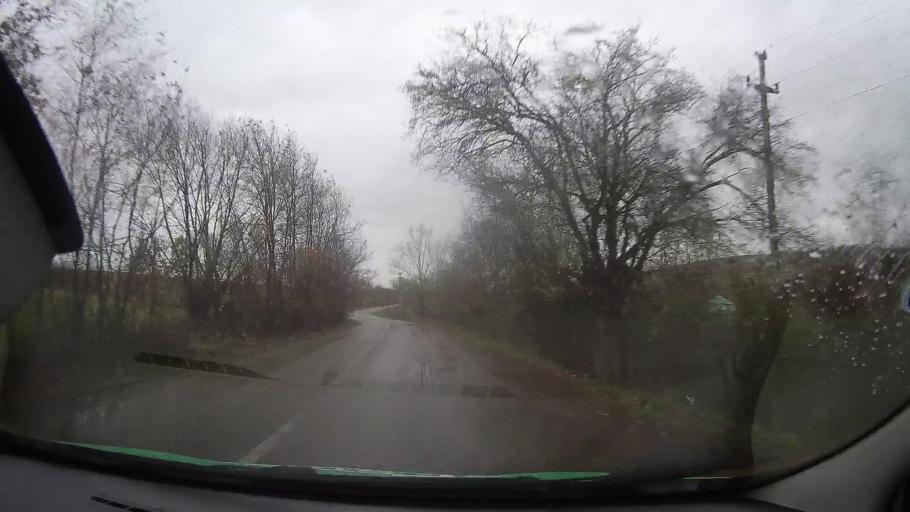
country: RO
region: Mures
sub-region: Comuna Brancovenesti
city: Valenii de Mures
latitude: 46.9198
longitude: 24.7765
